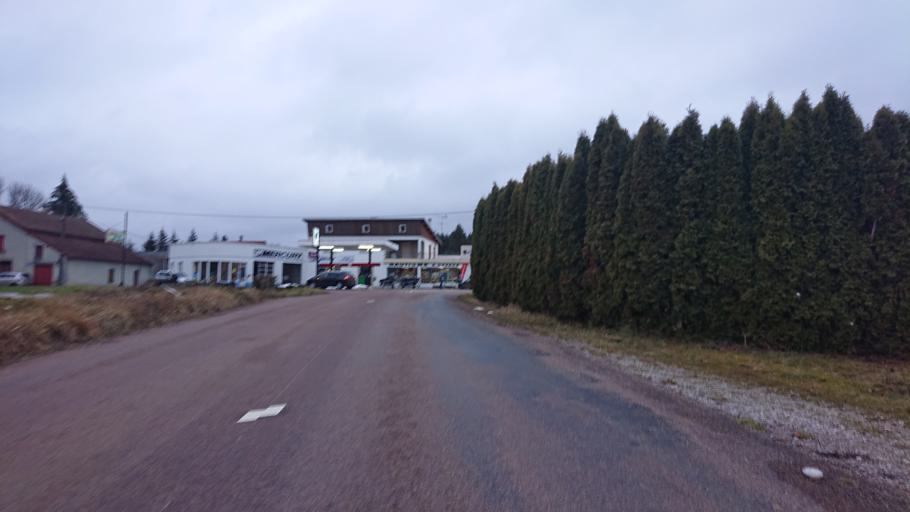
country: FR
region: Franche-Comte
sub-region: Departement du Jura
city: Clairvaux-les-Lacs
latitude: 46.5877
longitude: 5.6922
